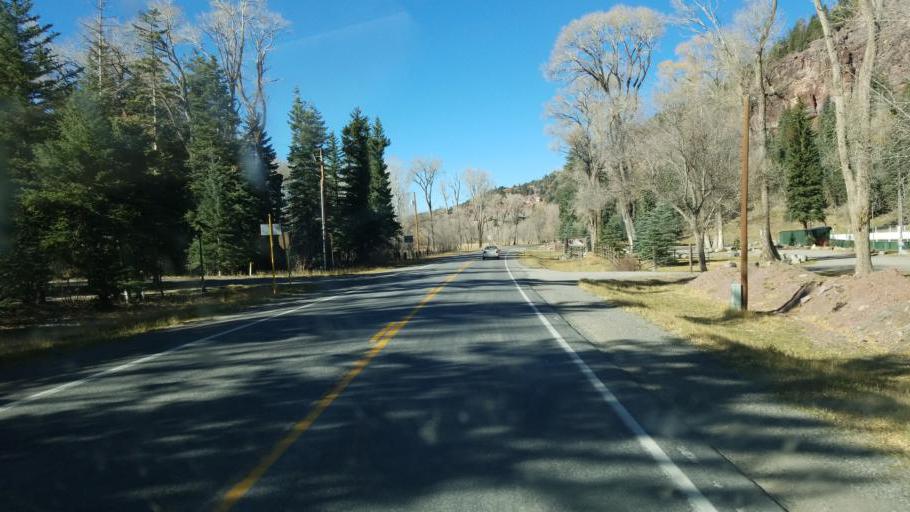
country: US
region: Colorado
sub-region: Ouray County
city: Ouray
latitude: 38.0434
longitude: -107.6813
